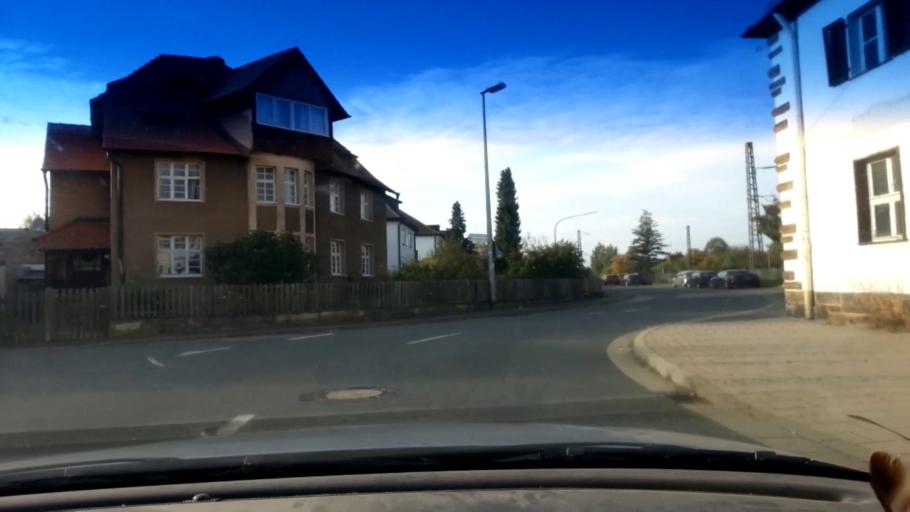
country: DE
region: Bavaria
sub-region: Upper Franconia
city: Hirschaid
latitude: 49.8194
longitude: 10.9907
